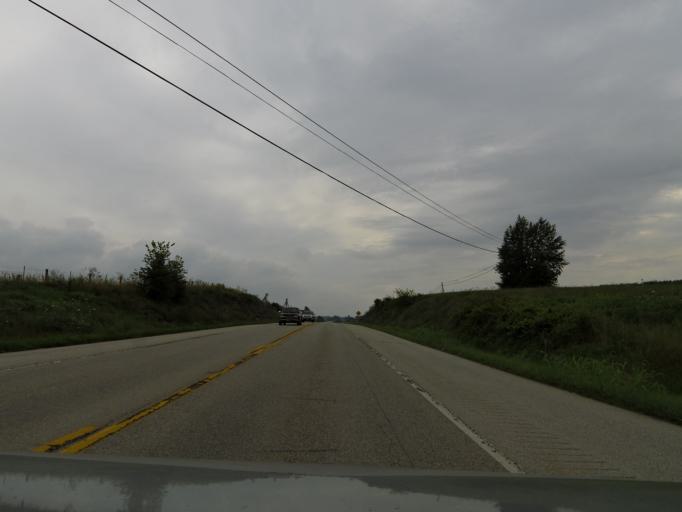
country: US
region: Kentucky
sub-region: Mason County
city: Maysville
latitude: 38.5295
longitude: -83.8320
